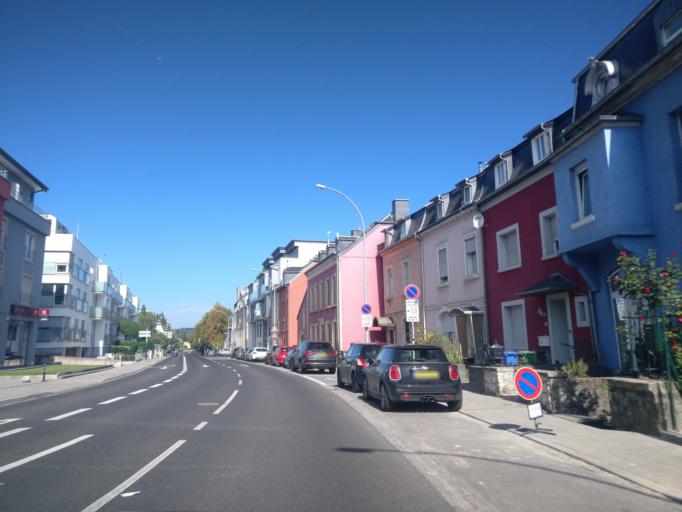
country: LU
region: Luxembourg
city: Kirchberg
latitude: 49.6335
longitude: 6.1355
